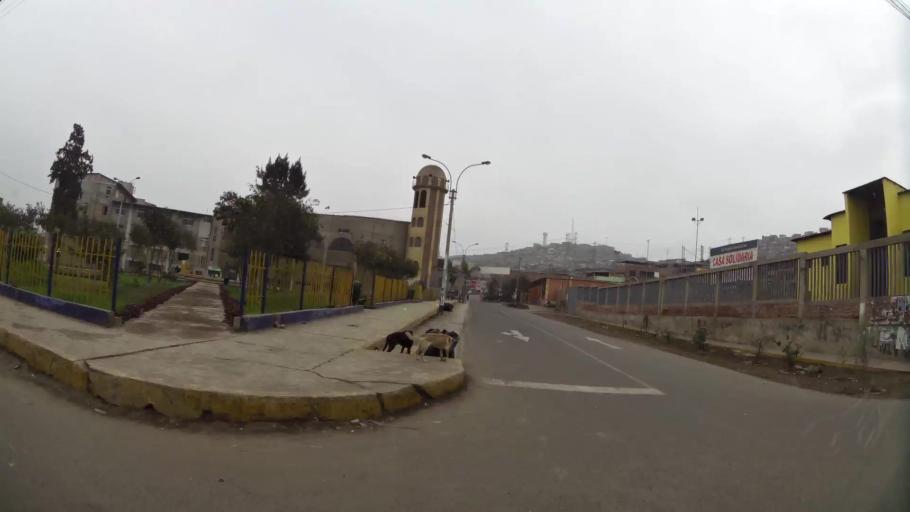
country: PE
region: Lima
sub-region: Lima
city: Surco
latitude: -12.1793
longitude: -76.9484
